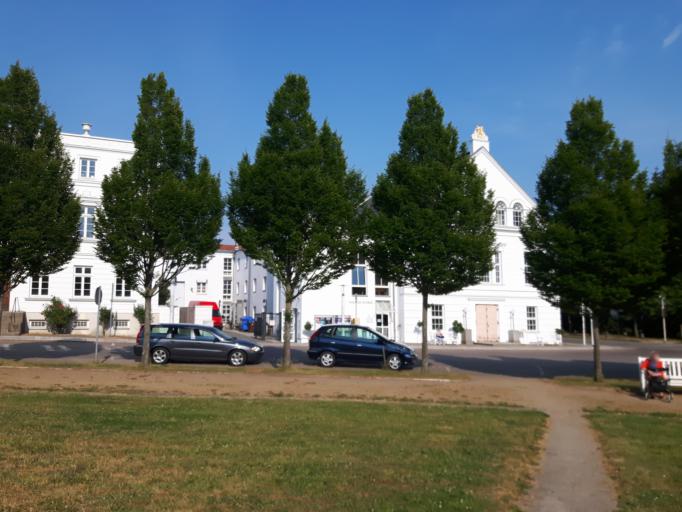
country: DE
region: Mecklenburg-Vorpommern
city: Putbus
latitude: 54.3529
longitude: 13.4687
